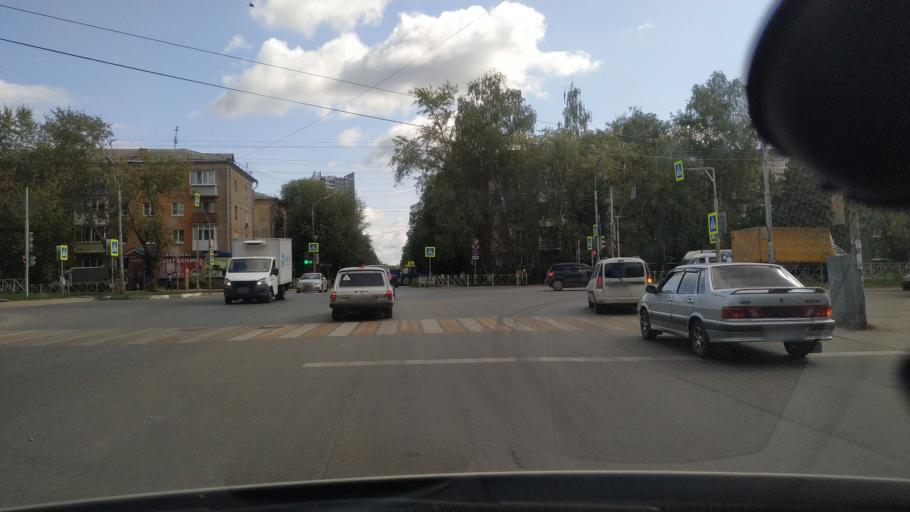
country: RU
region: Rjazan
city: Ryazan'
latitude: 54.6057
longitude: 39.7117
